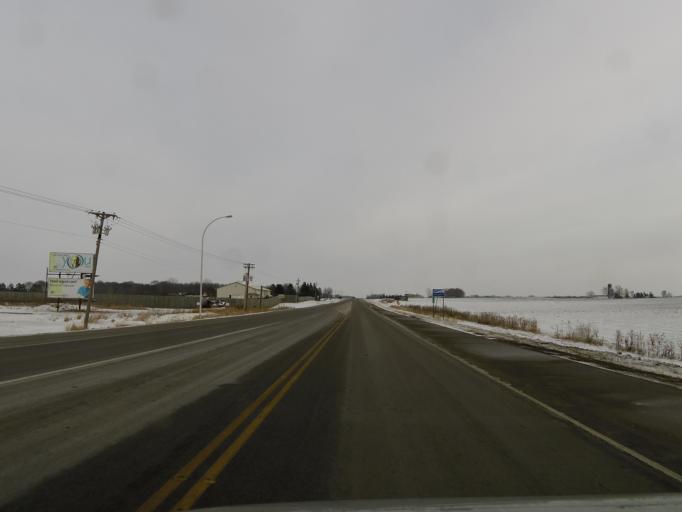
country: US
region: Minnesota
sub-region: McLeod County
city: Lester Prairie
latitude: 44.9063
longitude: -94.0323
